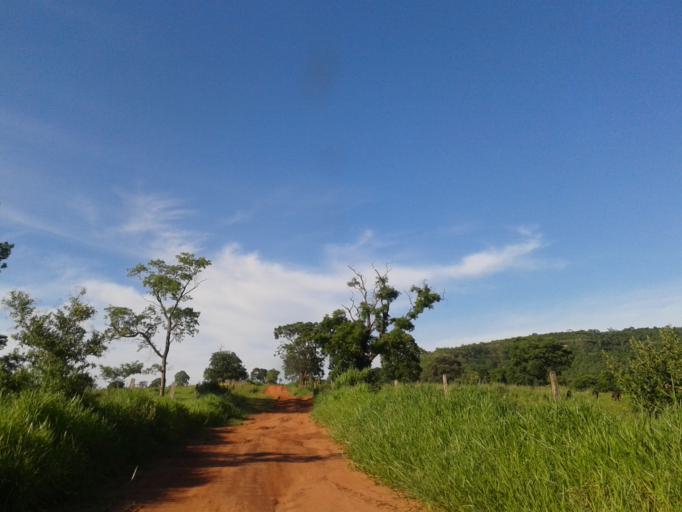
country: BR
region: Minas Gerais
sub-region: Santa Vitoria
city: Santa Vitoria
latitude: -19.0867
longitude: -49.9640
